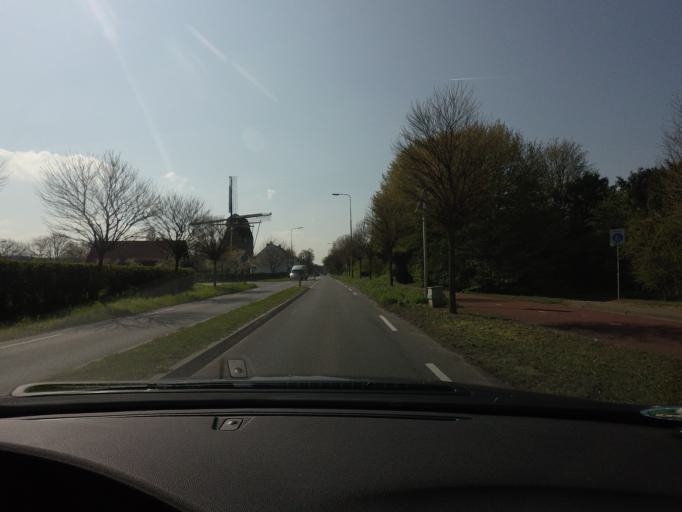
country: NL
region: Limburg
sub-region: Gemeente Maastricht
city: Heer
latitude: 50.8253
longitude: 5.7293
